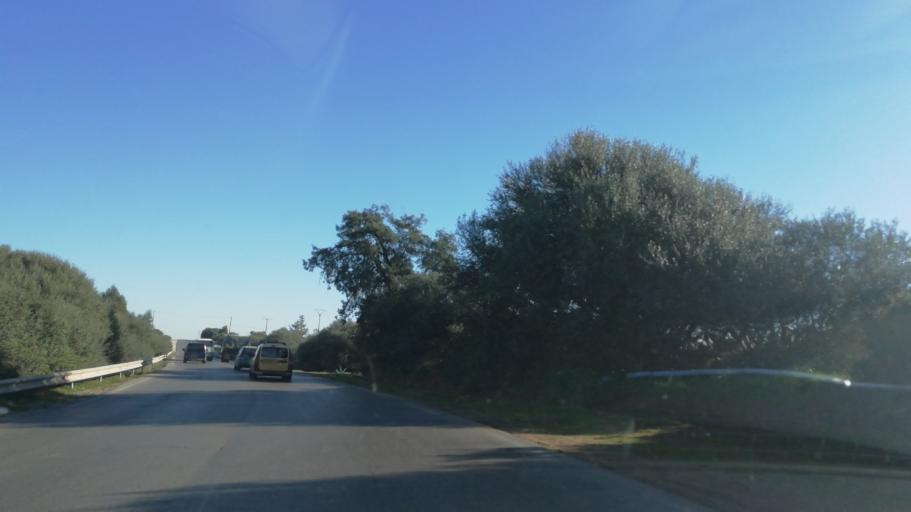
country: DZ
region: Relizane
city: Smala
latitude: 35.6938
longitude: 0.7830
